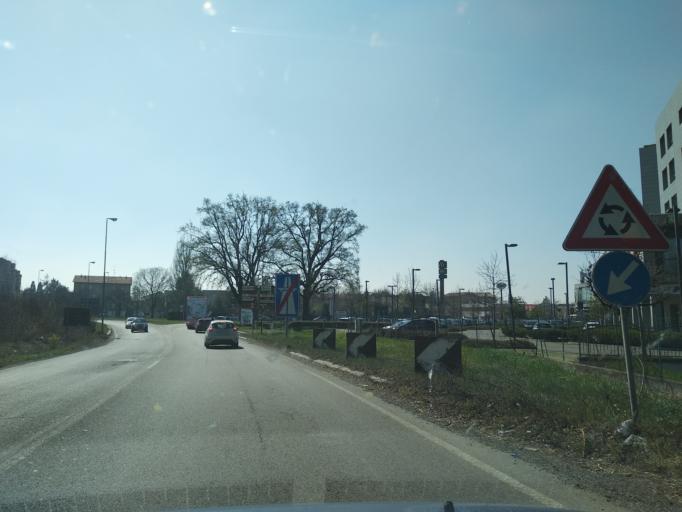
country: IT
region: Emilia-Romagna
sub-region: Provincia di Reggio Emilia
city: Reggio nell'Emilia
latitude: 44.7120
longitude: 10.6194
